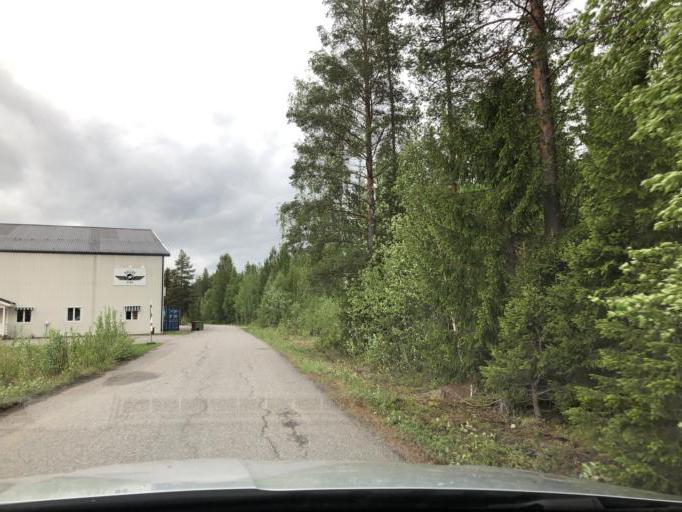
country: SE
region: Norrbotten
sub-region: Pitea Kommun
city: Roknas
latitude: 65.3910
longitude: 21.2696
